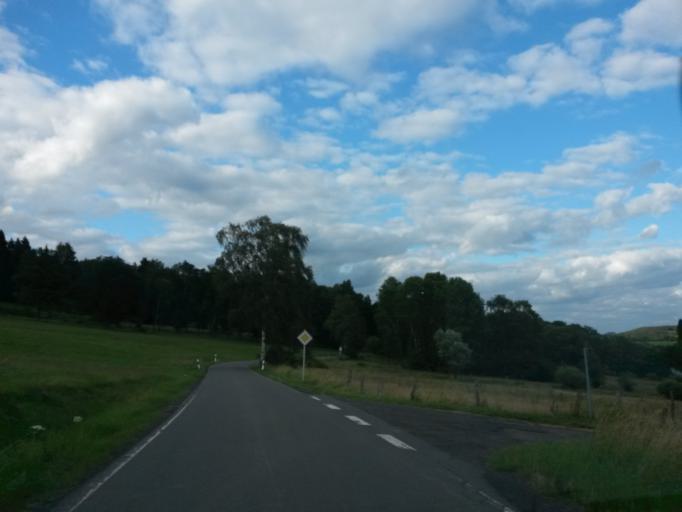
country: DE
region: North Rhine-Westphalia
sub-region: Regierungsbezirk Arnsberg
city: Drolshagen
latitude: 51.0961
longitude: 7.7366
